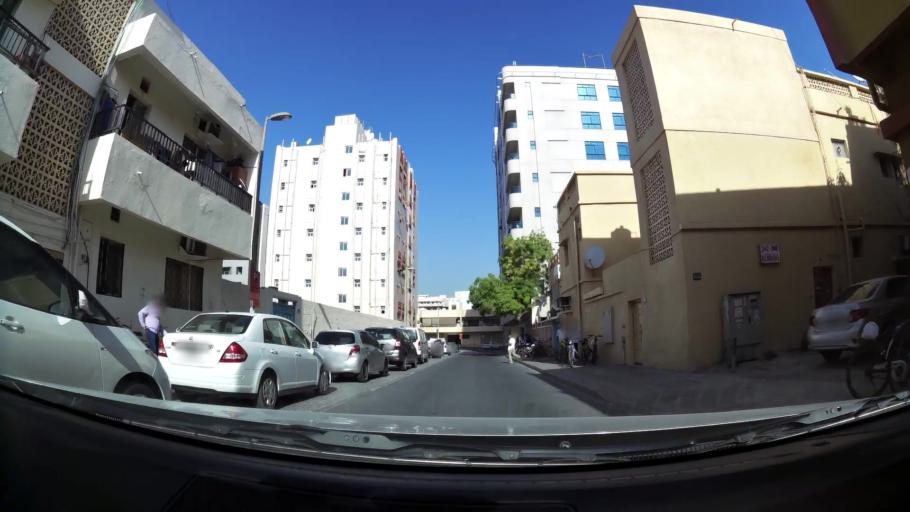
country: AE
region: Ash Shariqah
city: Sharjah
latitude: 25.2580
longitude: 55.2912
